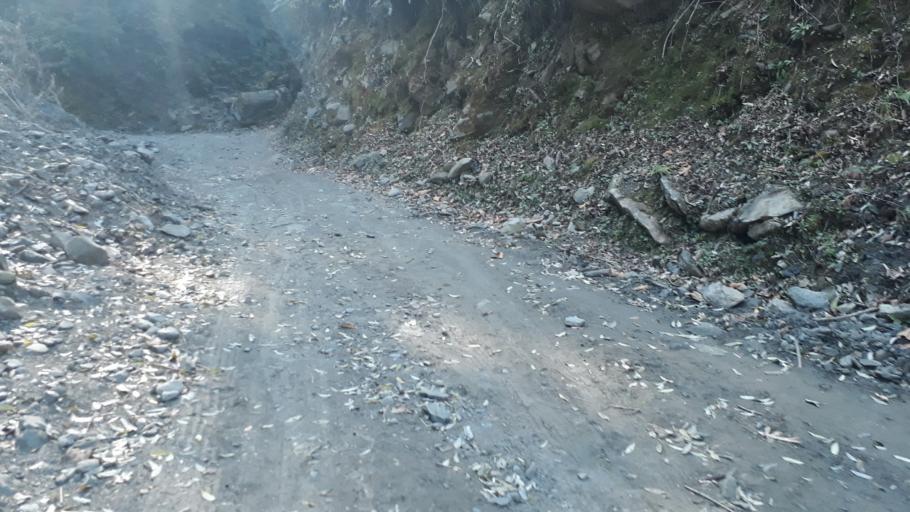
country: IN
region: Himachal Pradesh
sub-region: Mandi
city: Pandoh
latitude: 31.7749
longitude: 77.0893
